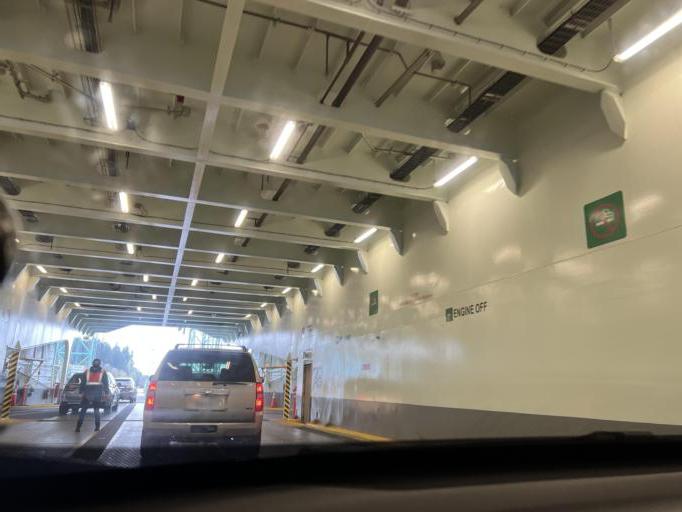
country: US
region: Washington
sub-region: Snohomish County
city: Mukilteo
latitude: 47.9739
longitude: -122.3489
